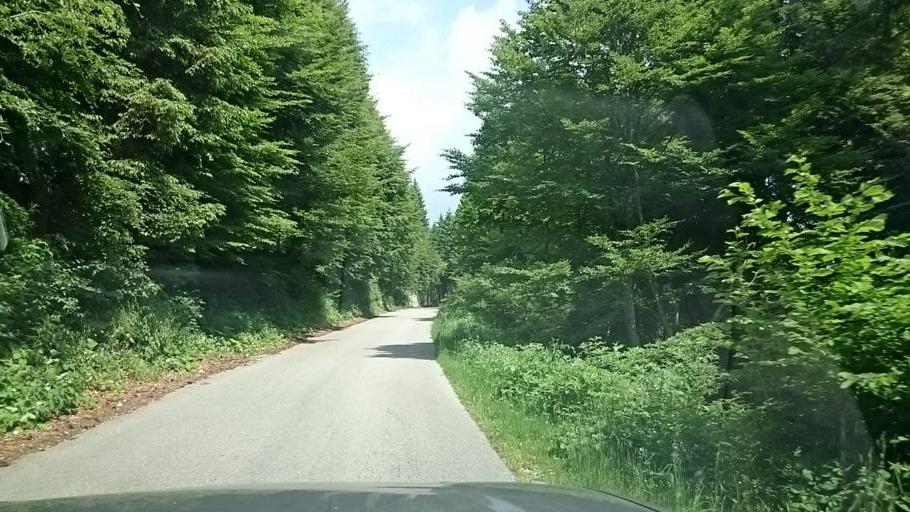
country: IT
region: Veneto
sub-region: Provincia di Vicenza
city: Foza
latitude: 45.9170
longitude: 11.6460
